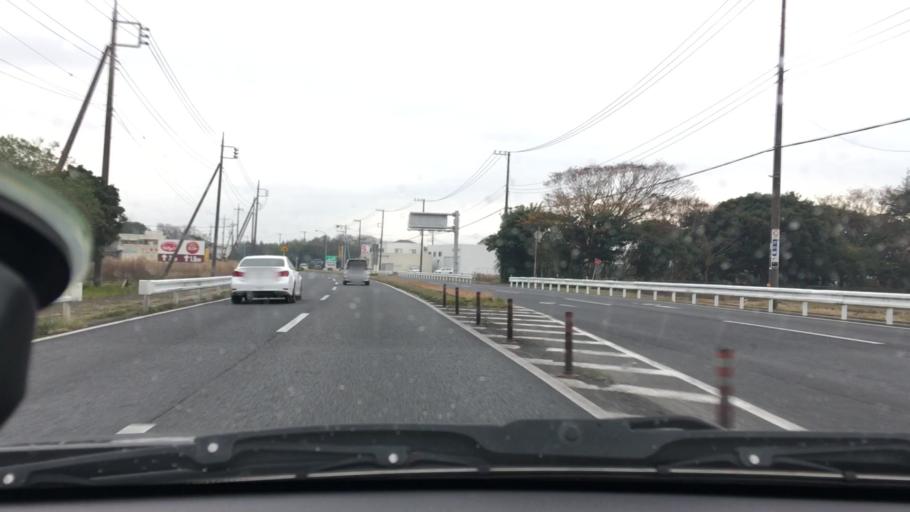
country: JP
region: Chiba
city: Omigawa
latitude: 35.9076
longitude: 140.6233
